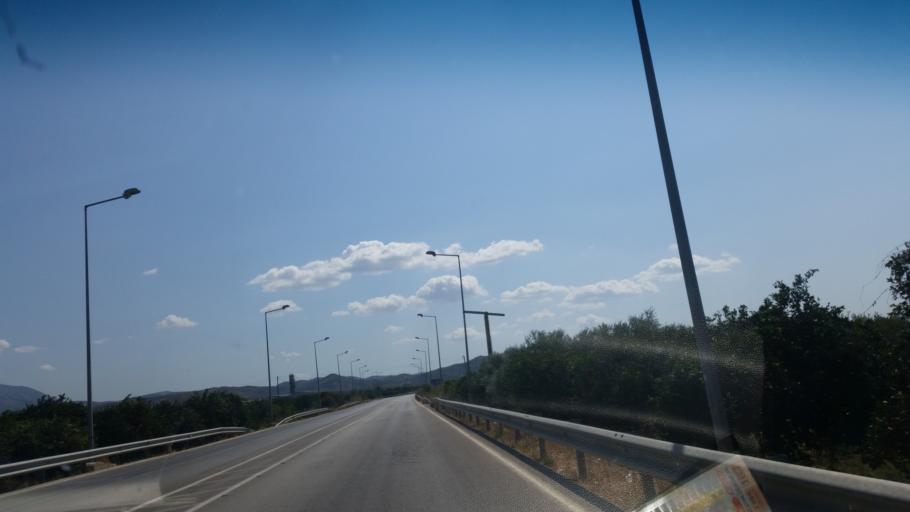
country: GR
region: Peloponnese
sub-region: Nomos Argolidos
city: Ayia Trias
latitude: 37.6432
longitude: 22.8111
